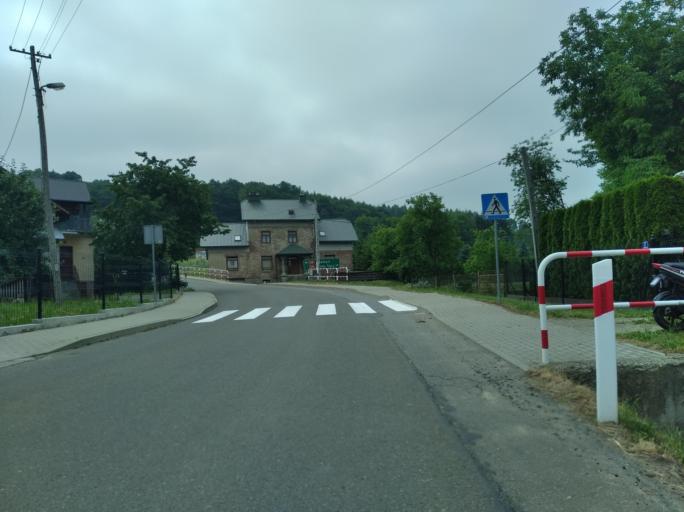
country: PL
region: Subcarpathian Voivodeship
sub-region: Powiat sanocki
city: Besko
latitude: 49.5888
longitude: 21.9463
